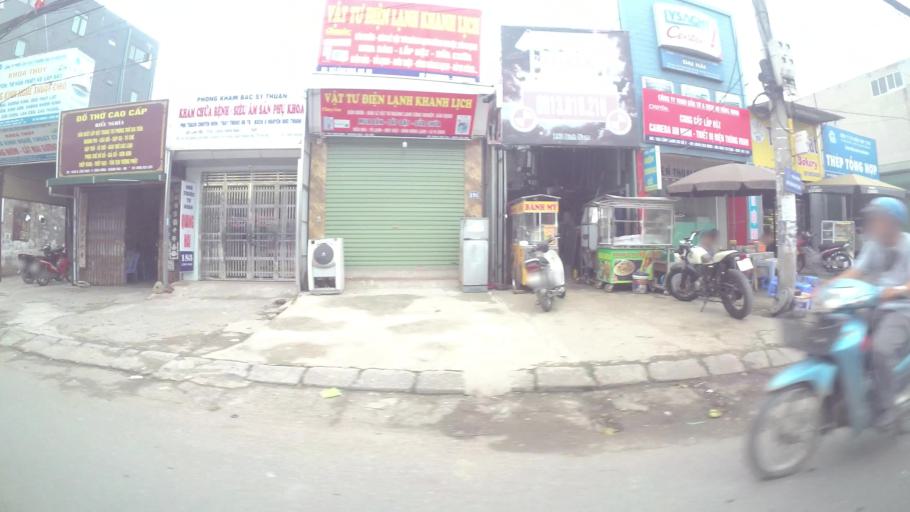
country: VN
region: Ha Noi
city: Hai BaTrung
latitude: 20.9855
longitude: 105.8707
